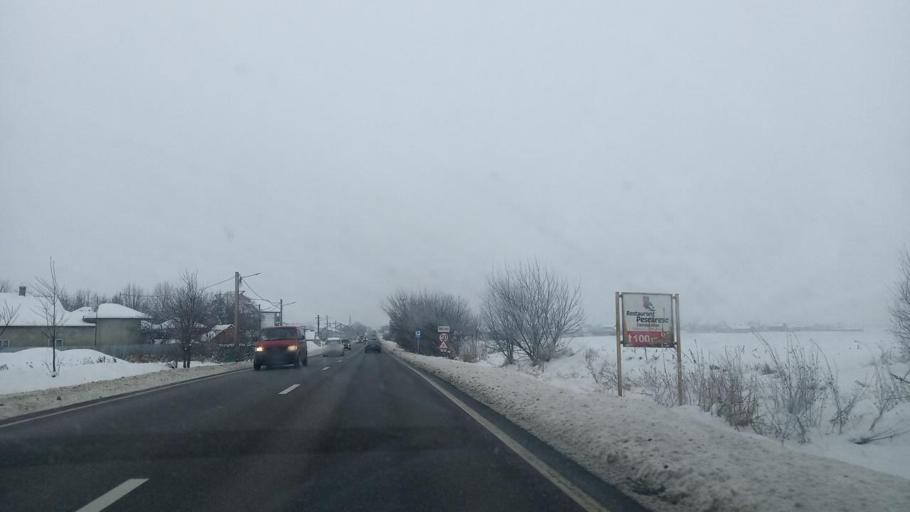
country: RO
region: Neamt
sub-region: Comuna Sabaoani
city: Sabaoani
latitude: 47.0332
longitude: 26.8505
